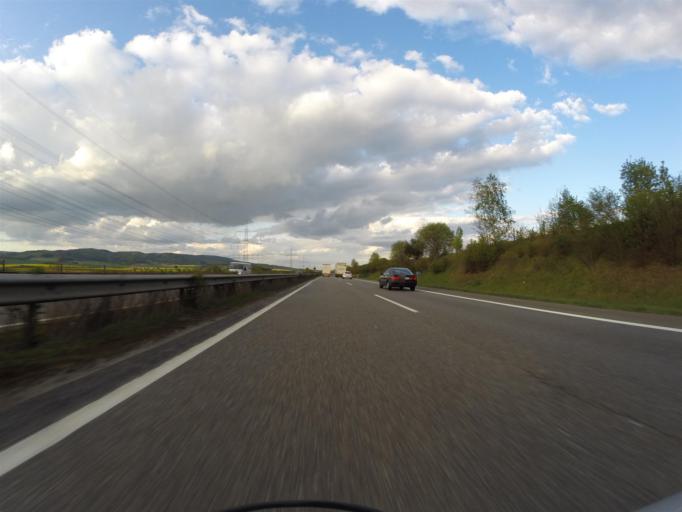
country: DE
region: Rheinland-Pfalz
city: Lohnsfeld
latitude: 49.5513
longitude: 7.8653
